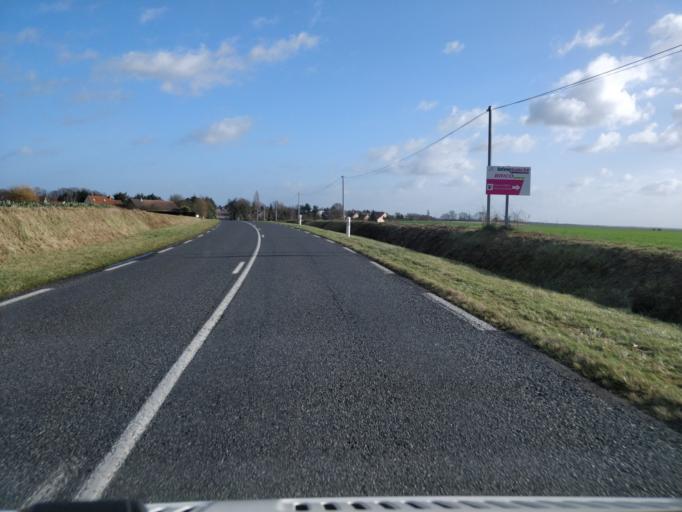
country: FR
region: Bourgogne
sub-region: Departement de l'Yonne
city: Cheroy
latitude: 48.2016
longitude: 2.9823
